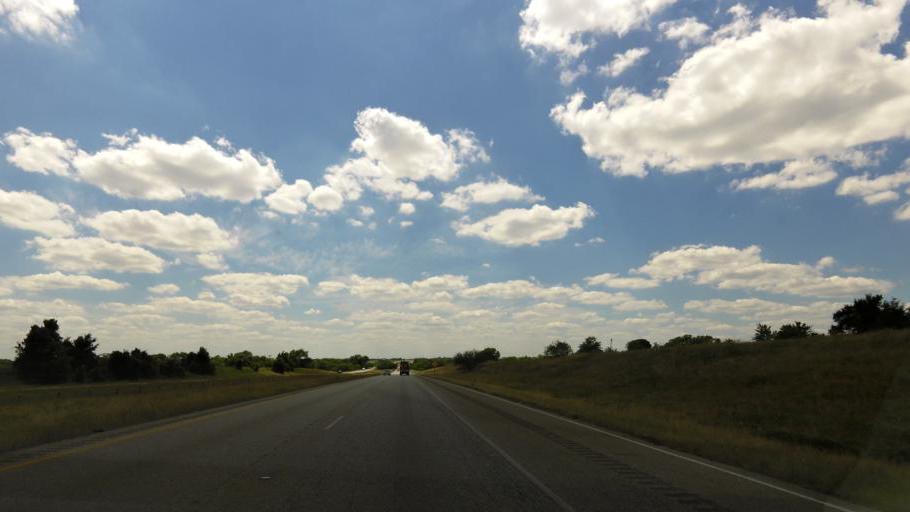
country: US
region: Texas
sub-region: Fayette County
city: Schulenburg
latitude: 29.6902
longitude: -96.9330
